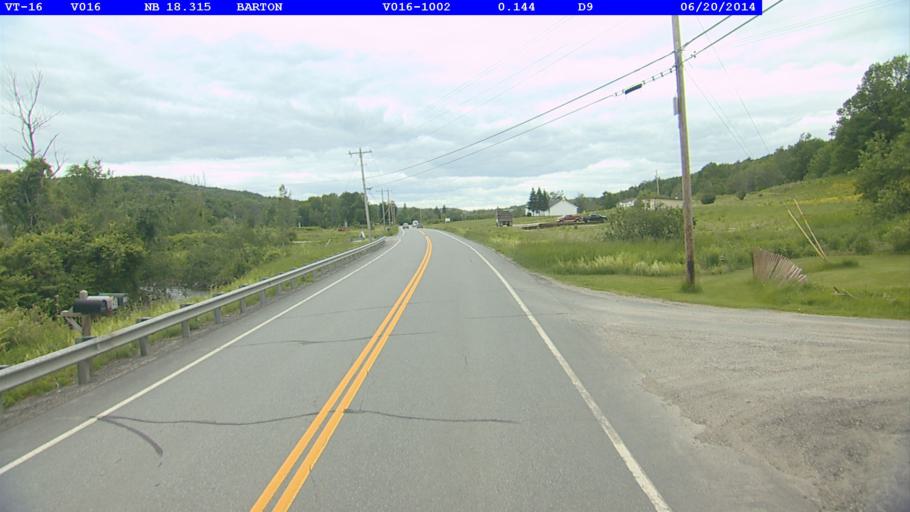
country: US
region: Vermont
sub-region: Orleans County
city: Newport
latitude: 44.7194
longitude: -72.1848
